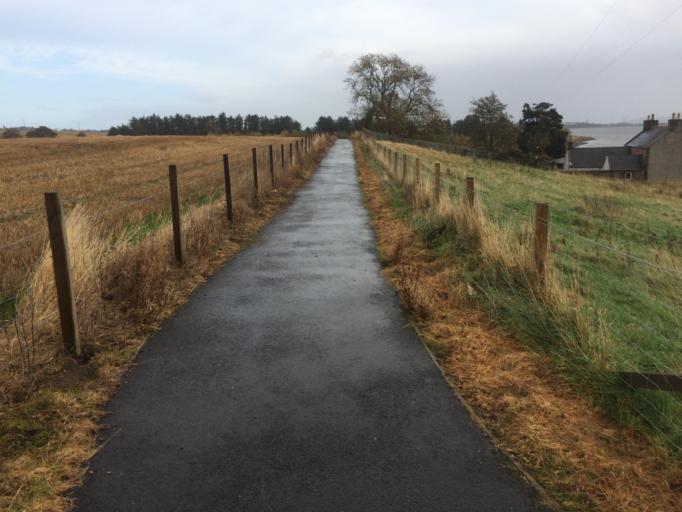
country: GB
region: Scotland
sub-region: Highland
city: Alness
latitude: 57.6910
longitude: -4.2294
